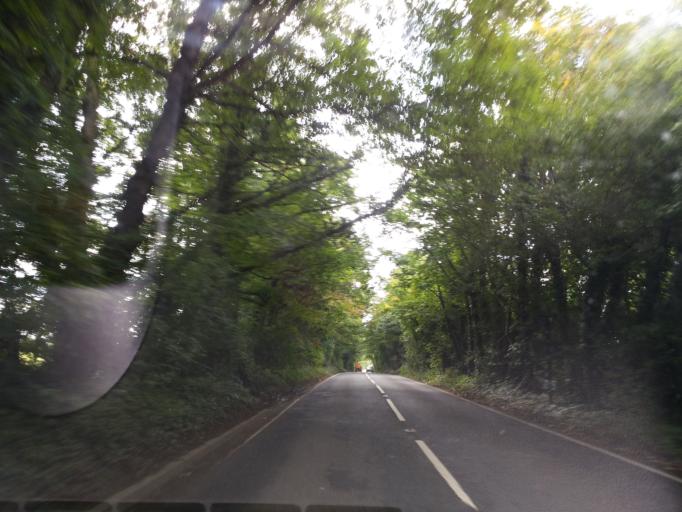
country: GB
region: England
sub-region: Bath and North East Somerset
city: Hinton Charterhouse
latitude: 51.3305
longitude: -2.3175
